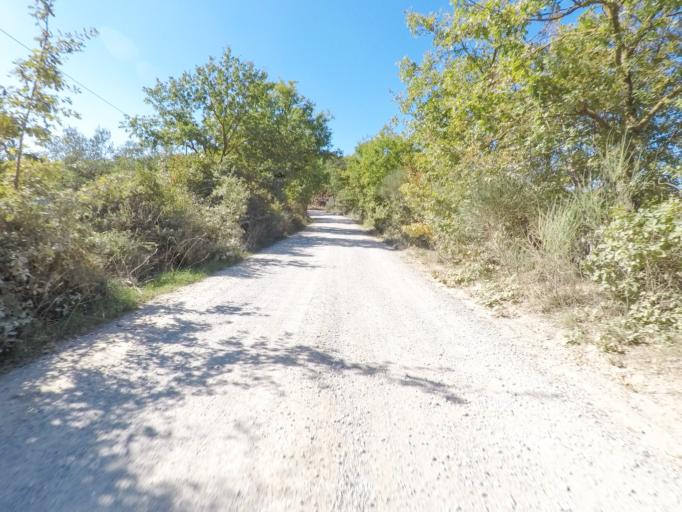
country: IT
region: Tuscany
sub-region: Provincia di Siena
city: Castellina in Chianti
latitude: 43.4361
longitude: 11.3230
